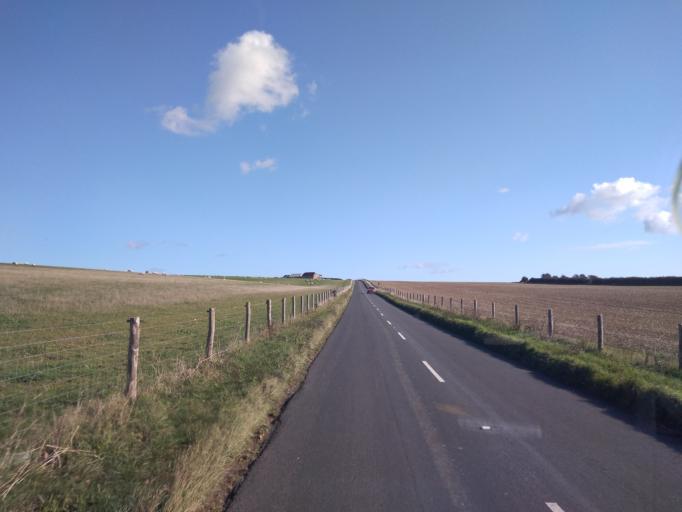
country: GB
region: England
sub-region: East Sussex
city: Seaford
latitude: 50.7848
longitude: 0.1298
